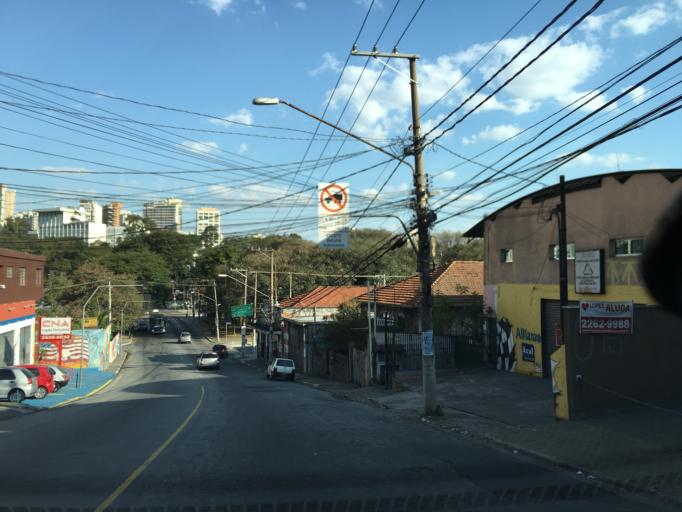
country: BR
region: Sao Paulo
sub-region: Sao Paulo
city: Sao Paulo
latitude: -23.4812
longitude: -46.6321
